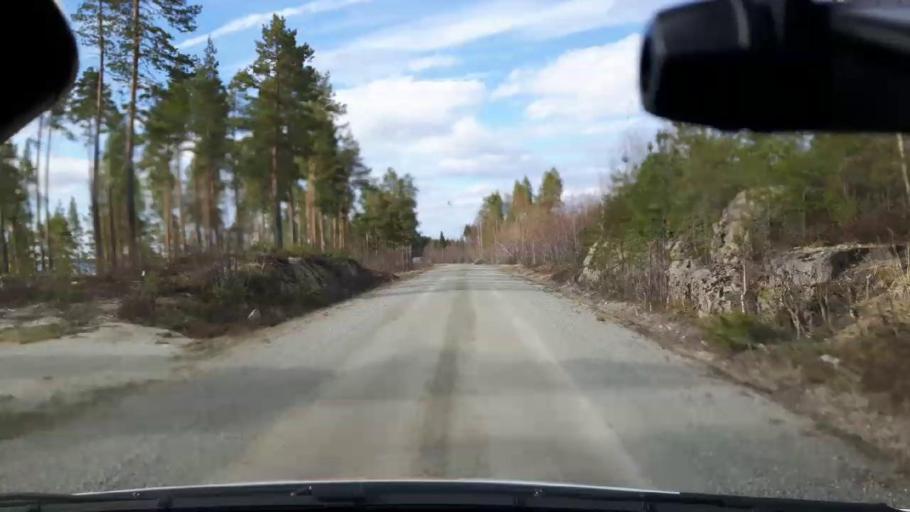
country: SE
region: Jaemtland
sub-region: Bergs Kommun
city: Hoverberg
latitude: 62.7316
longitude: 14.6651
